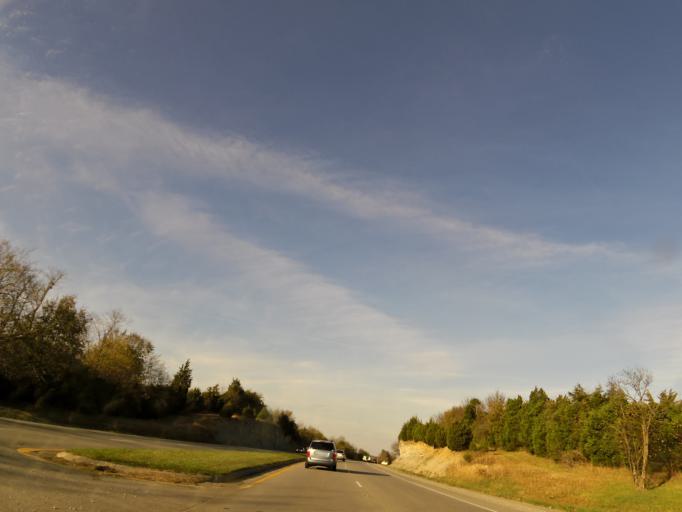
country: US
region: Kentucky
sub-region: Lincoln County
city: Stanford
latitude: 37.5209
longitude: -84.6586
